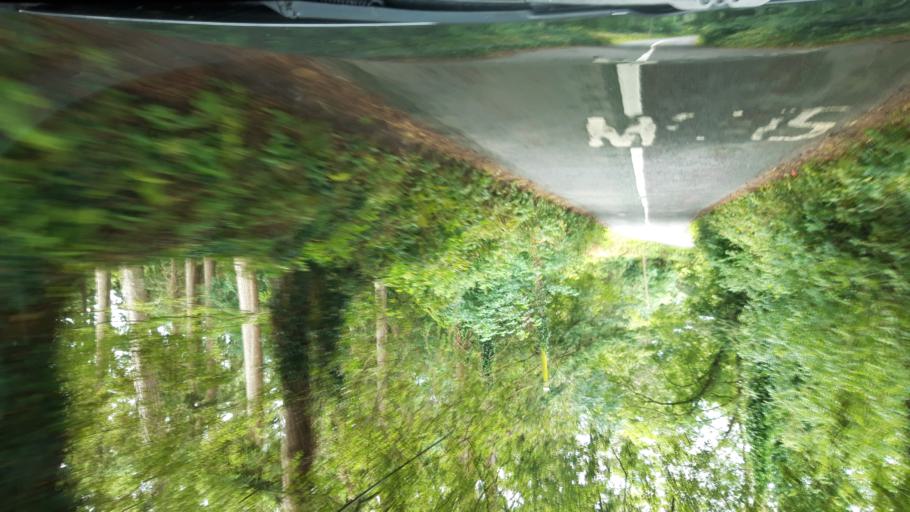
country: IE
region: Munster
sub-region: County Cork
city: Castlemartyr
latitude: 52.1309
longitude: -8.0068
